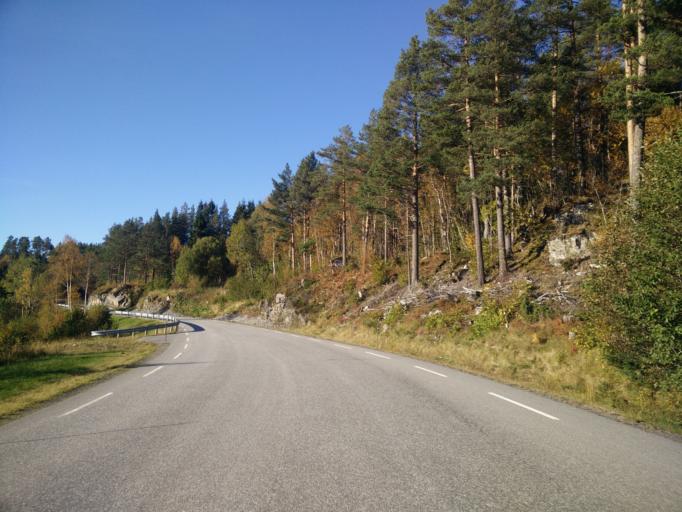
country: NO
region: More og Romsdal
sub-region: Halsa
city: Liaboen
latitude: 63.1008
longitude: 8.3423
